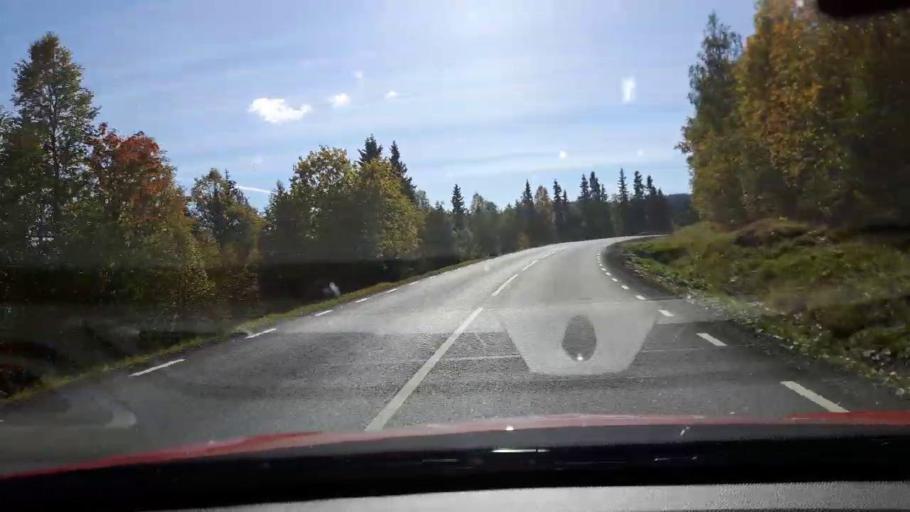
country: NO
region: Nord-Trondelag
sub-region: Royrvik
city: Royrvik
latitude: 64.8747
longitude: 14.2110
